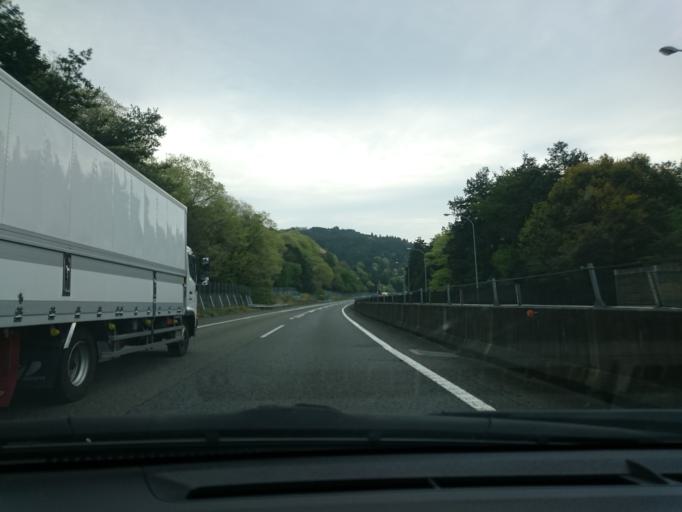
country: JP
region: Gifu
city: Tarui
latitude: 35.3523
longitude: 136.4822
